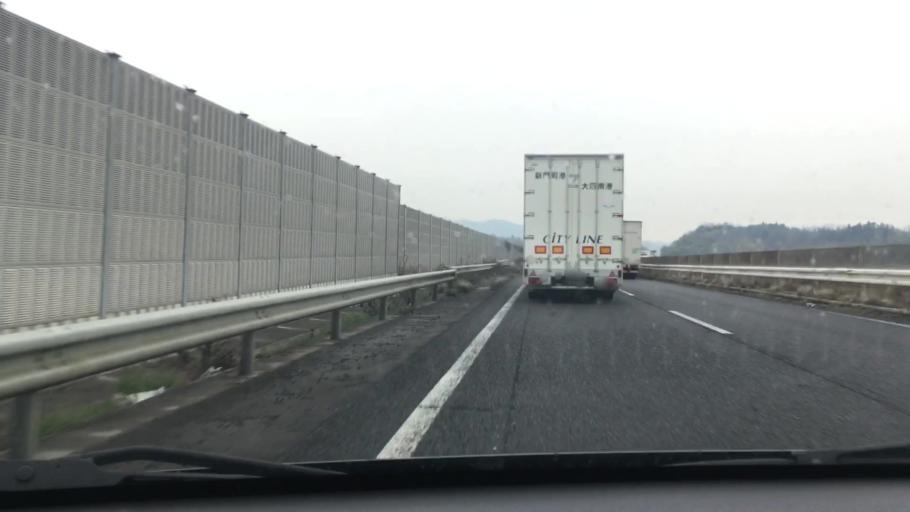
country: JP
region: Mie
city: Ueno-ebisumachi
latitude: 34.7770
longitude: 136.1576
